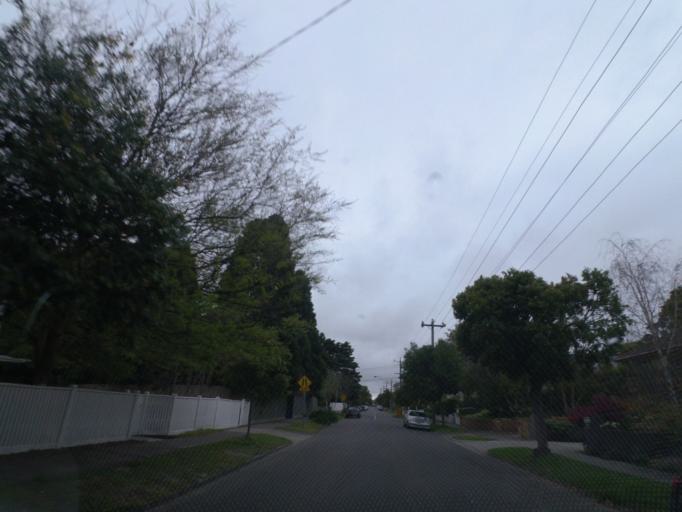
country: AU
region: Victoria
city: Carnegie
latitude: -37.8735
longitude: 145.0713
